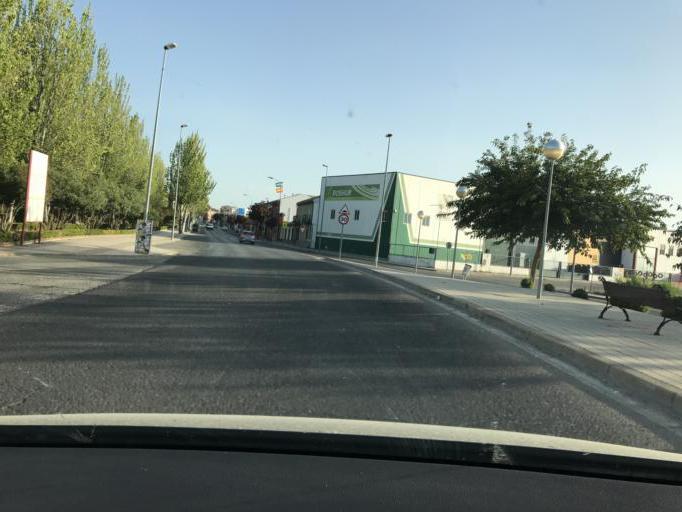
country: ES
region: Andalusia
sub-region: Provincia de Jaen
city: Ubeda
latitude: 38.0246
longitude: -3.3709
